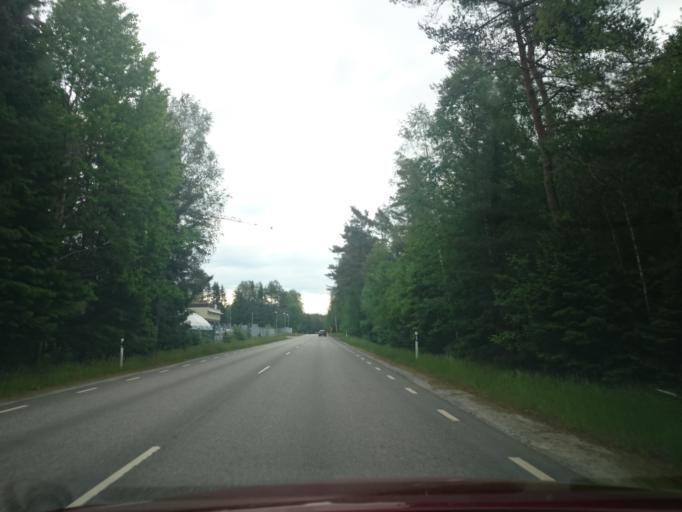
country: SE
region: Vaestra Goetaland
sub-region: Harryda Kommun
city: Hindas
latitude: 57.6973
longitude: 12.3665
